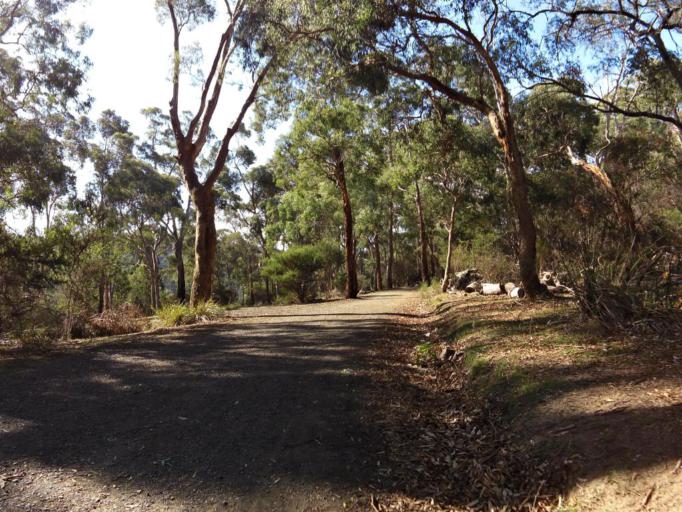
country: AU
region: Victoria
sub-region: Casey
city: Endeavour Hills
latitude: -37.9516
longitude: 145.2522
